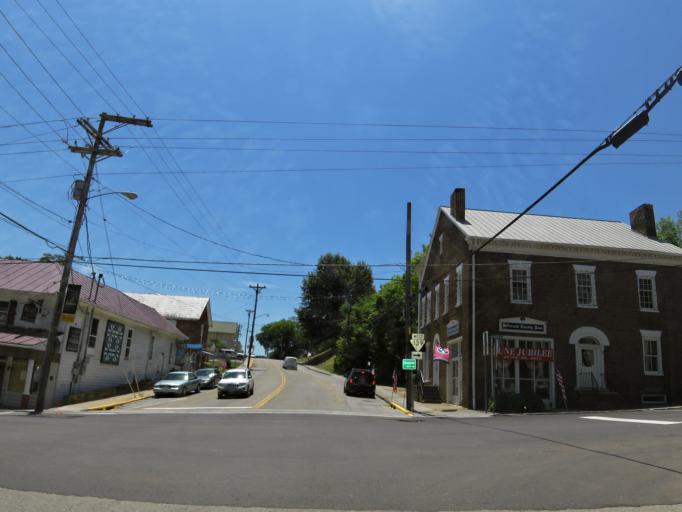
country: US
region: Tennessee
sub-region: Jefferson County
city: Dandridge
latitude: 36.0153
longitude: -83.4151
